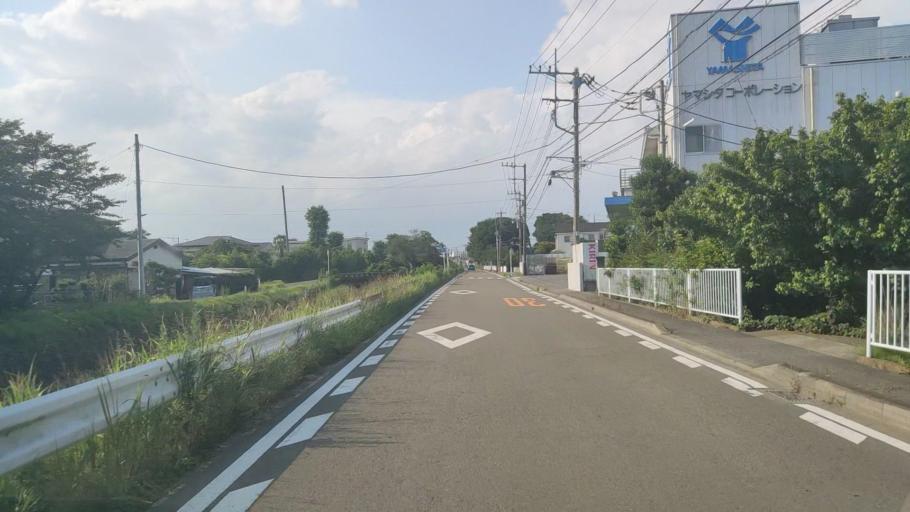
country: JP
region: Kanagawa
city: Isehara
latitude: 35.3876
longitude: 139.3386
